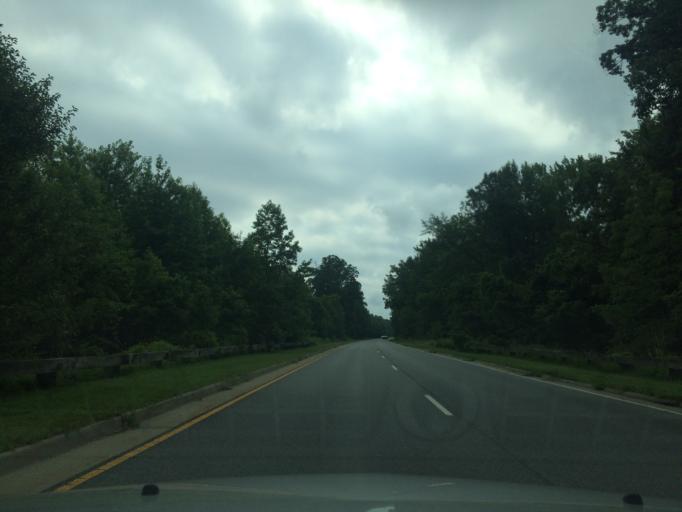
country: US
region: Maryland
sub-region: Prince George's County
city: Morningside
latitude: 38.8354
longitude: -76.8909
